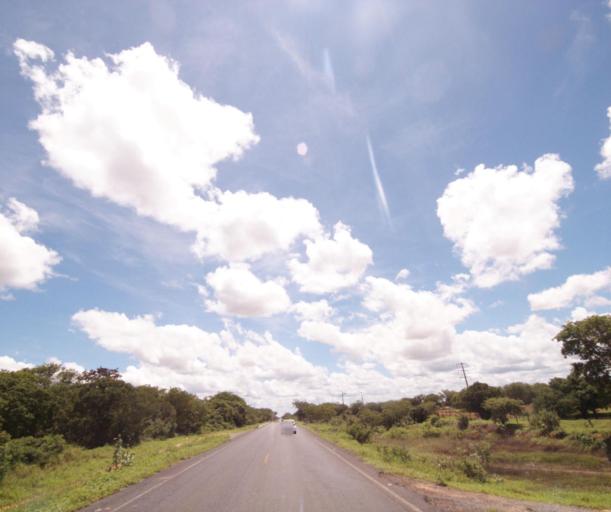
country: BR
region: Bahia
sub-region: Bom Jesus Da Lapa
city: Bom Jesus da Lapa
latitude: -13.2593
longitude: -43.4894
